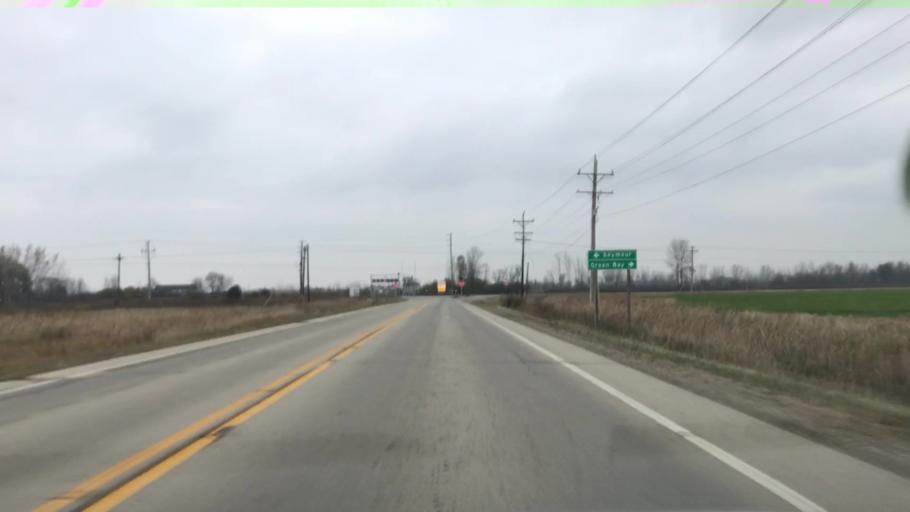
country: US
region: Wisconsin
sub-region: Outagamie County
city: Seymour
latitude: 44.4987
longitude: -88.2912
